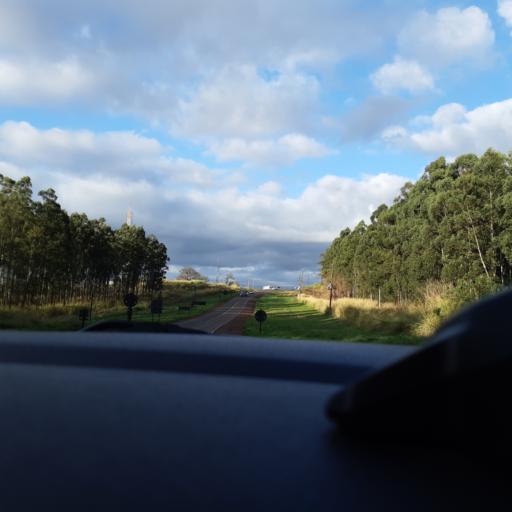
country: BR
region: Sao Paulo
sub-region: Ourinhos
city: Ourinhos
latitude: -22.9953
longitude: -49.8506
